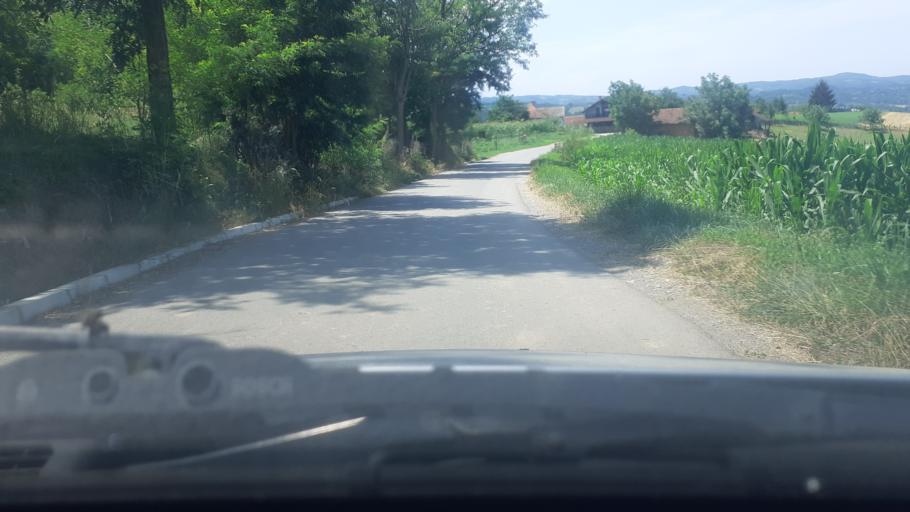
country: RS
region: Central Serbia
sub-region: Kolubarski Okrug
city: Osecina
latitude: 44.3916
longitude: 19.4965
